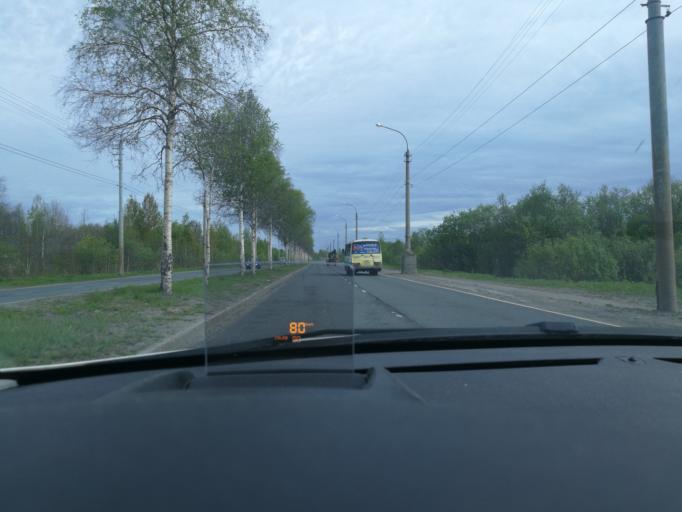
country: RU
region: Arkhangelskaya
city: Arkhangel'sk
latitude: 64.6044
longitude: 40.5249
